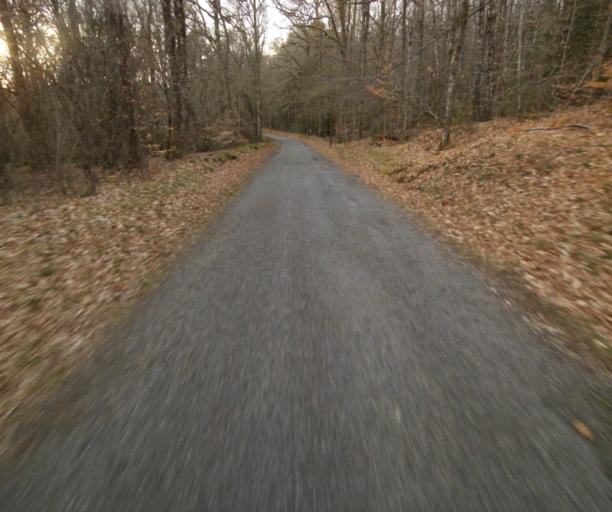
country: FR
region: Limousin
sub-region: Departement de la Correze
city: Correze
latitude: 45.2509
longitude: 1.9740
